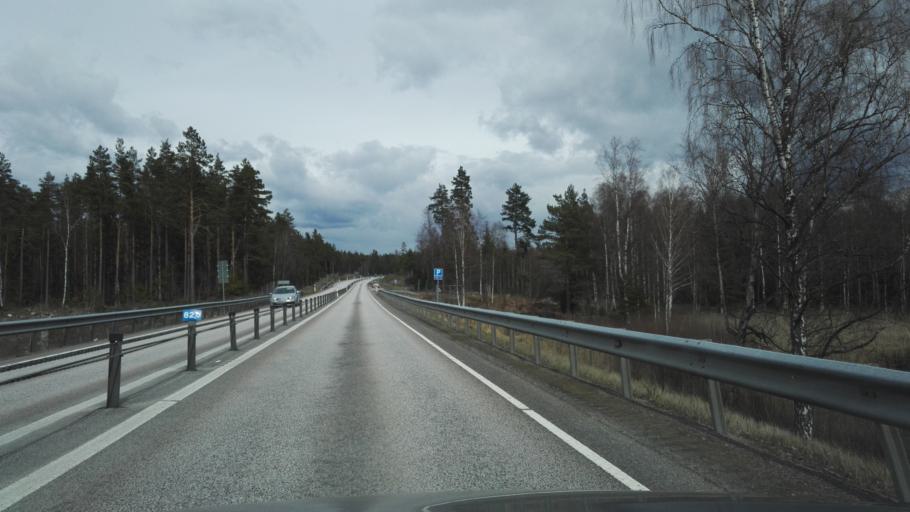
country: SE
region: Kronoberg
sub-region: Vaxjo Kommun
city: Braas
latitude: 56.9893
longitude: 14.9951
